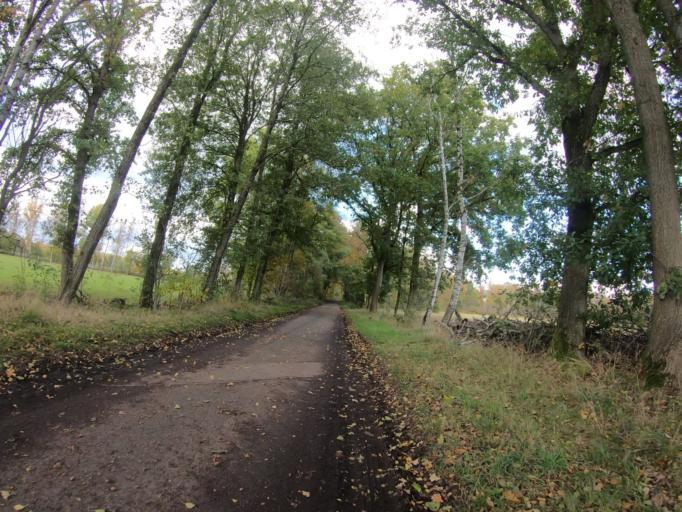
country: DE
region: Lower Saxony
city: Wagenhoff
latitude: 52.5442
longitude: 10.5654
